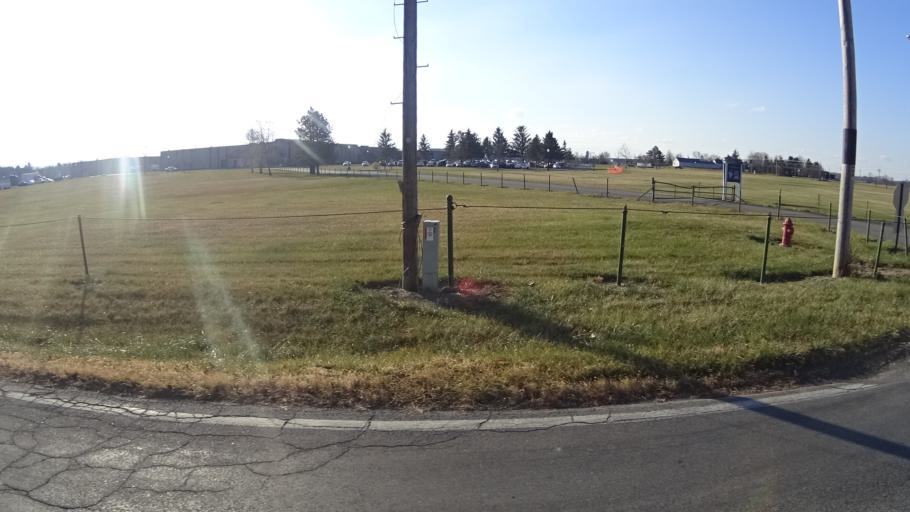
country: US
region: Ohio
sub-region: Lorain County
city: Oberlin
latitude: 41.2653
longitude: -82.2144
